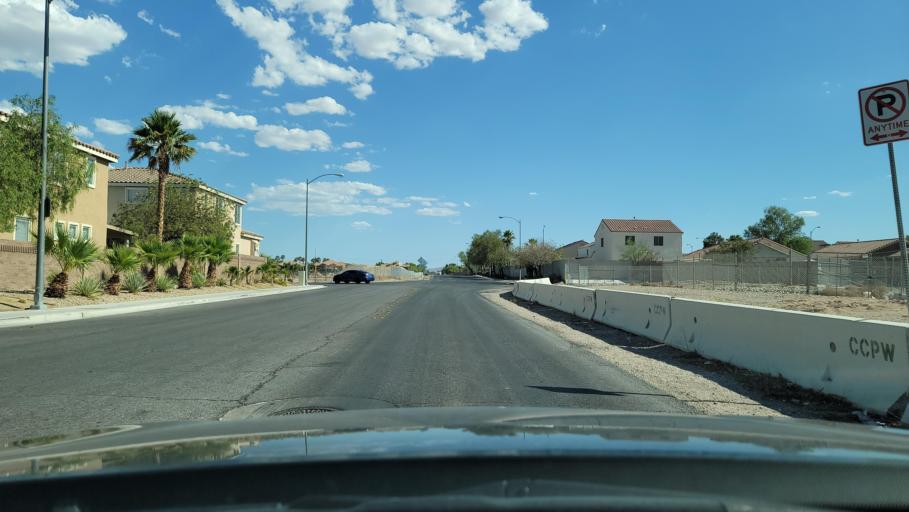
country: US
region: Nevada
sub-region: Clark County
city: Spring Valley
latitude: 36.0913
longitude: -115.2520
